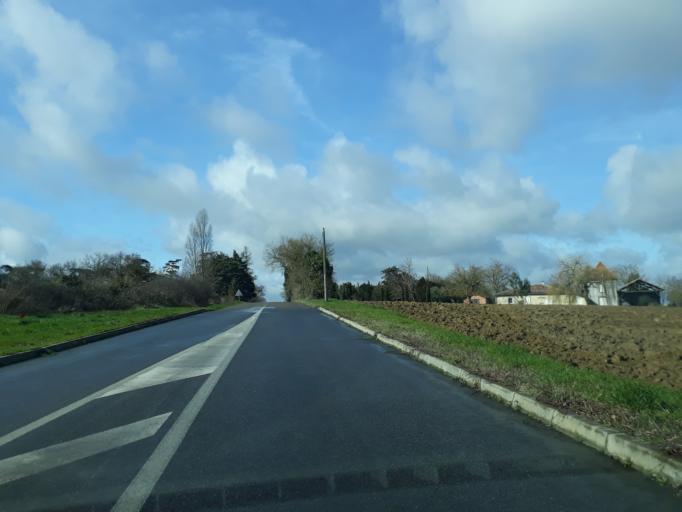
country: FR
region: Midi-Pyrenees
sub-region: Departement du Gers
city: Pujaudran
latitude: 43.6203
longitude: 1.0321
